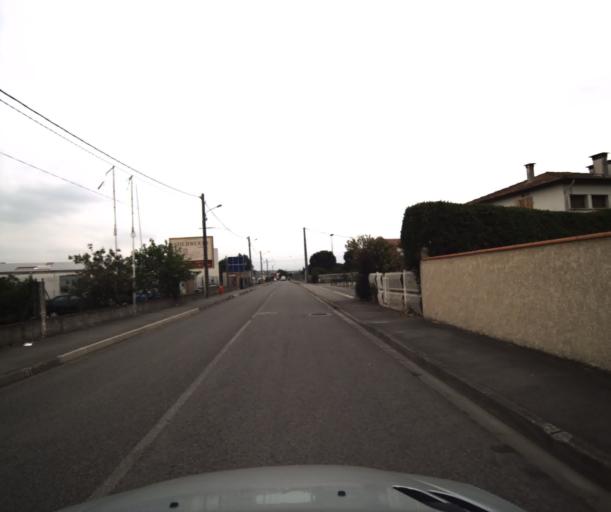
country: FR
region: Midi-Pyrenees
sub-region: Departement de la Haute-Garonne
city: Portet-sur-Garonne
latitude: 43.5389
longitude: 1.4025
